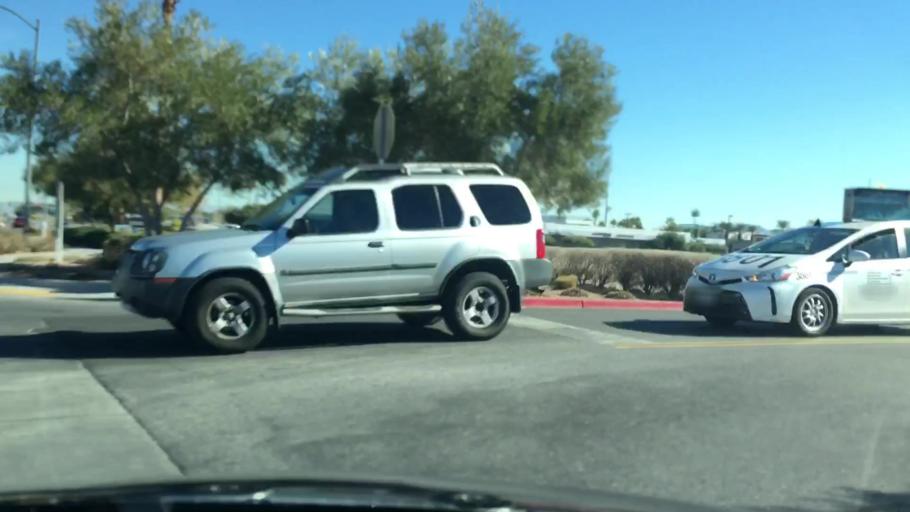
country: US
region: Nevada
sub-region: Clark County
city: Paradise
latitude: 36.0861
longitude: -115.1215
